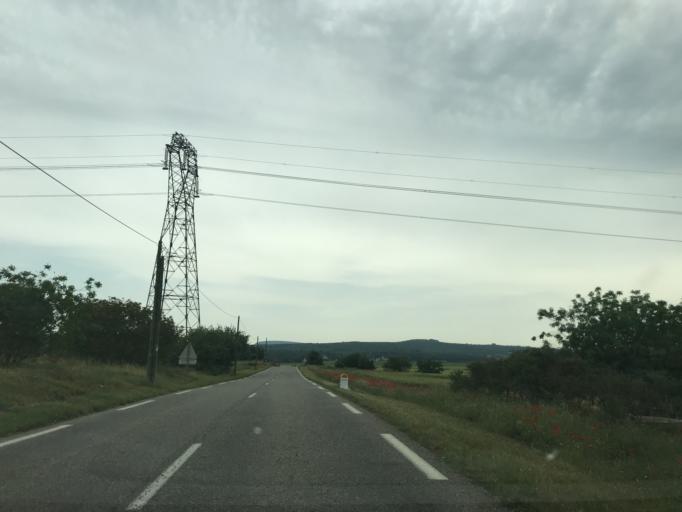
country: FR
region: Provence-Alpes-Cote d'Azur
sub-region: Departement du Var
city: Ginasservis
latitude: 43.6436
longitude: 5.8244
